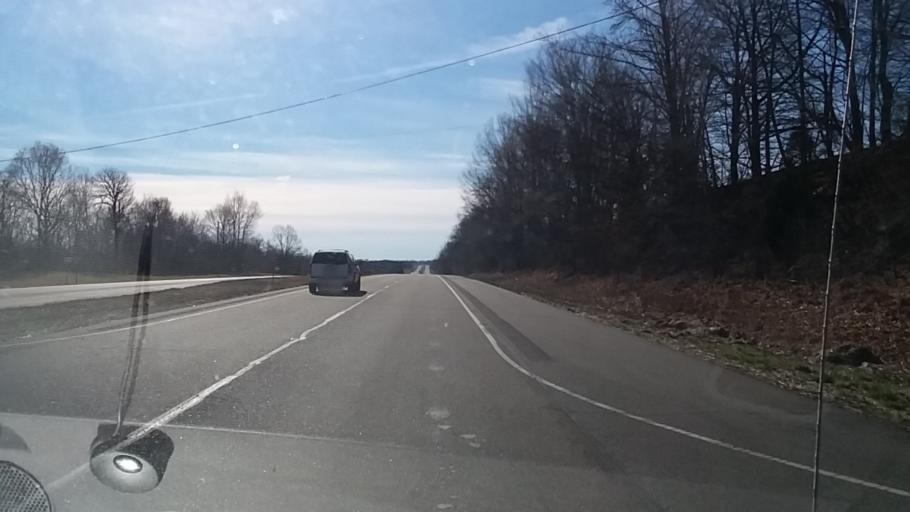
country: US
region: Tennessee
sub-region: Lauderdale County
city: Halls
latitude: 35.9093
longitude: -89.2614
